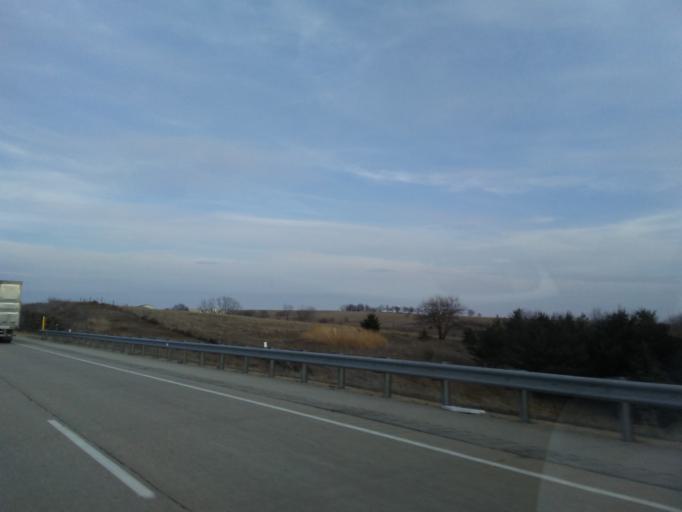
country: US
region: Wisconsin
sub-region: Iowa County
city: Barneveld
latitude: 43.0101
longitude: -89.8415
